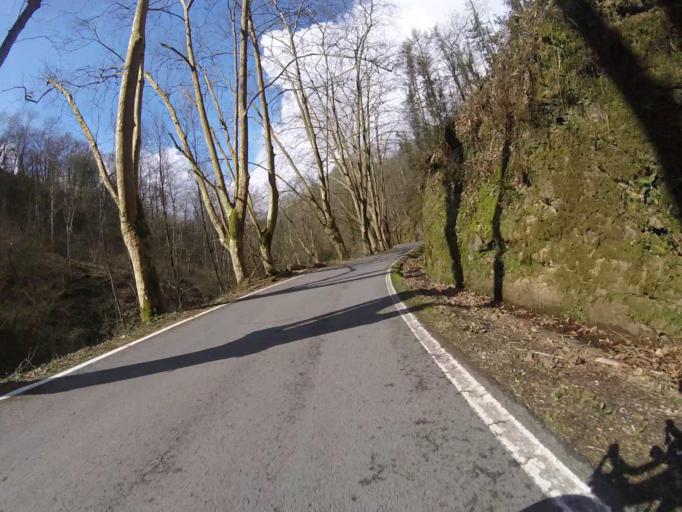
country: ES
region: Navarre
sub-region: Provincia de Navarra
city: Etxalar
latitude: 43.2474
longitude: -1.6198
